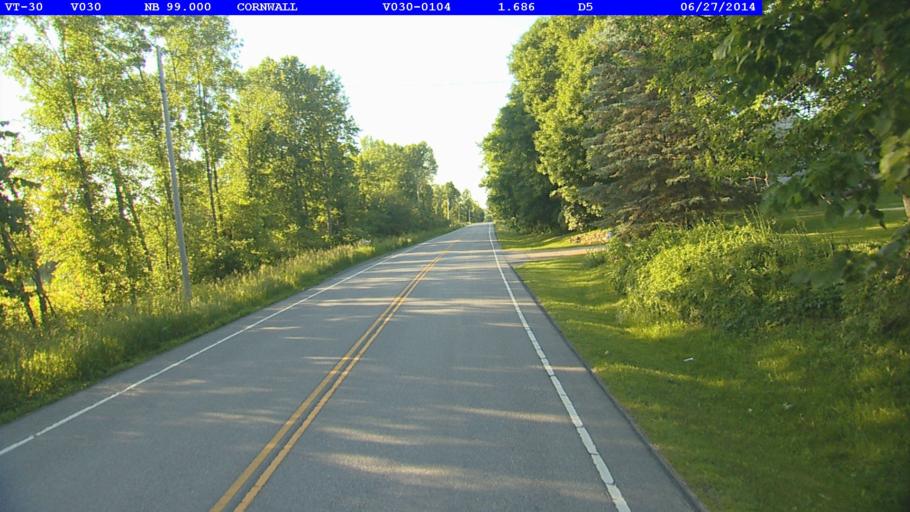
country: US
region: Vermont
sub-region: Addison County
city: Middlebury (village)
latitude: 43.9321
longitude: -73.2127
